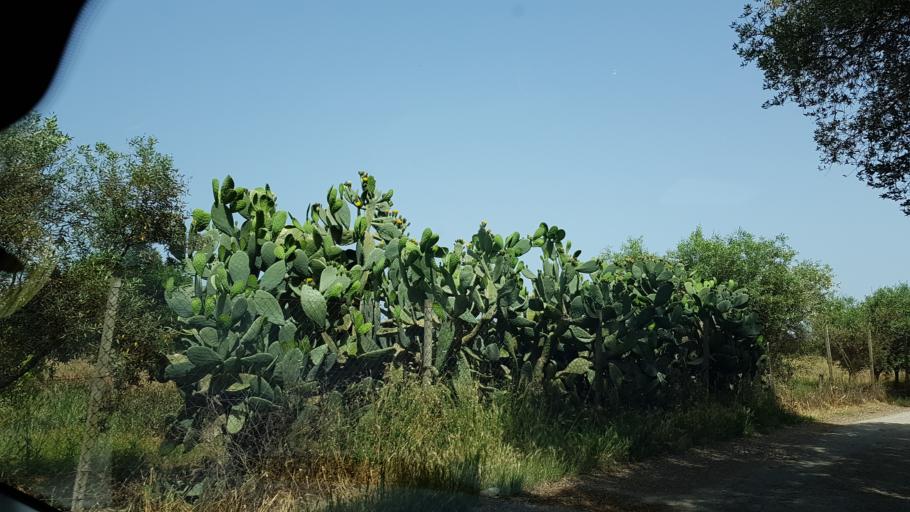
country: IT
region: Apulia
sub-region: Provincia di Brindisi
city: Mesagne
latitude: 40.5526
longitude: 17.8286
